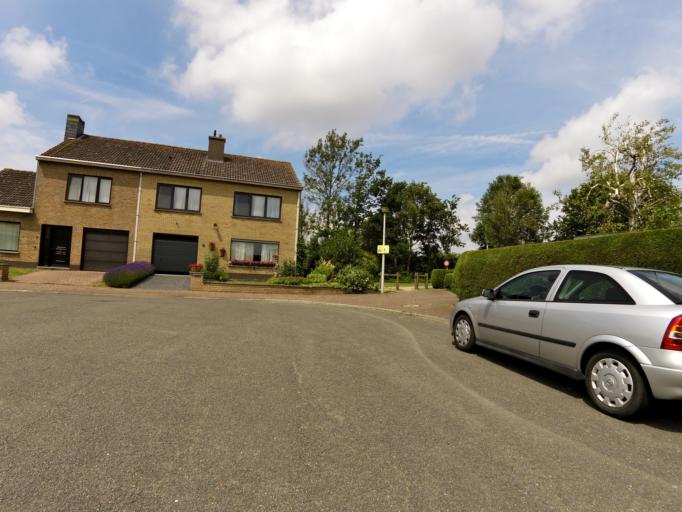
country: BE
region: Flanders
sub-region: Provincie West-Vlaanderen
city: Bredene
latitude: 51.2010
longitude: 2.9669
